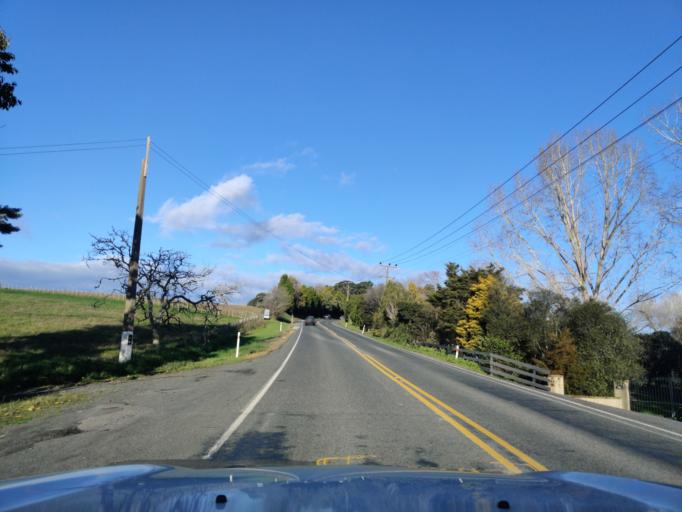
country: NZ
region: Auckland
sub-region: Auckland
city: Red Hill
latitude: -36.9640
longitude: 174.9798
